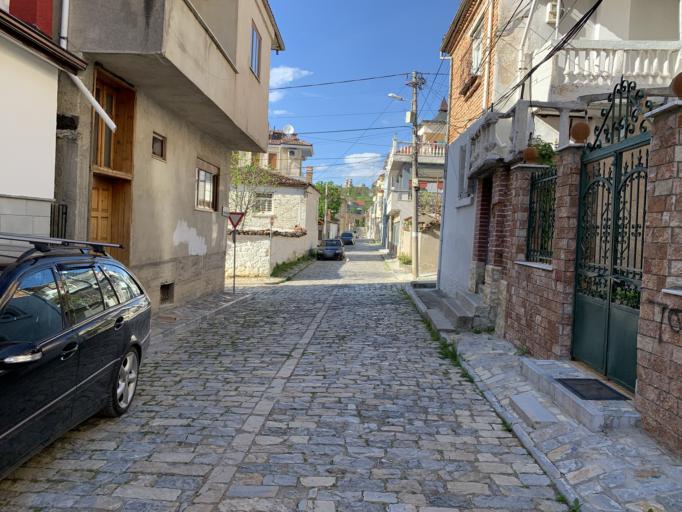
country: AL
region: Korce
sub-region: Rrethi i Korces
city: Korce
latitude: 40.6198
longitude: 20.7851
